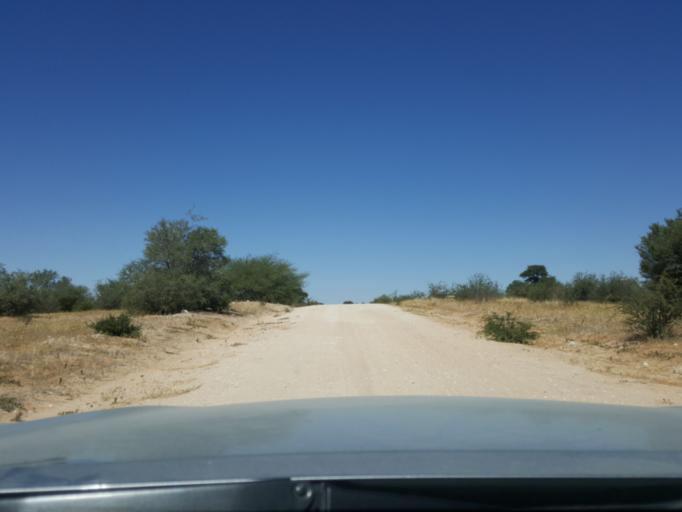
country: BW
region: Kgalagadi
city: Hukuntsi
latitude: -24.0108
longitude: 21.2140
